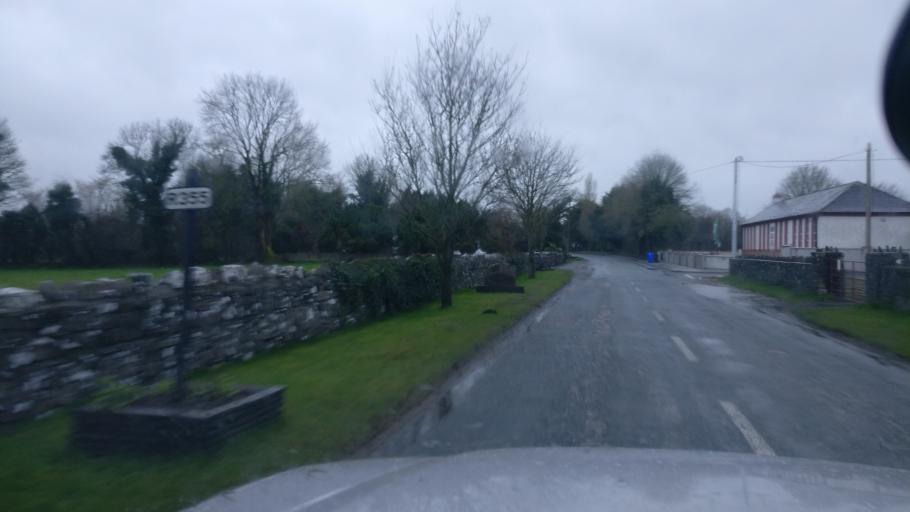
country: IE
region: Connaught
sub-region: County Galway
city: Ballinasloe
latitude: 53.2398
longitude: -8.1724
